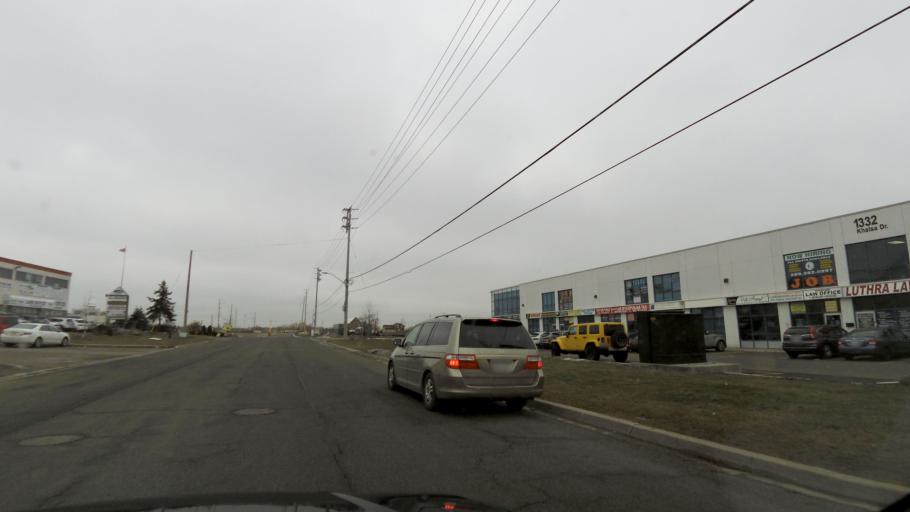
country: CA
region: Ontario
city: Brampton
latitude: 43.6737
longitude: -79.6788
